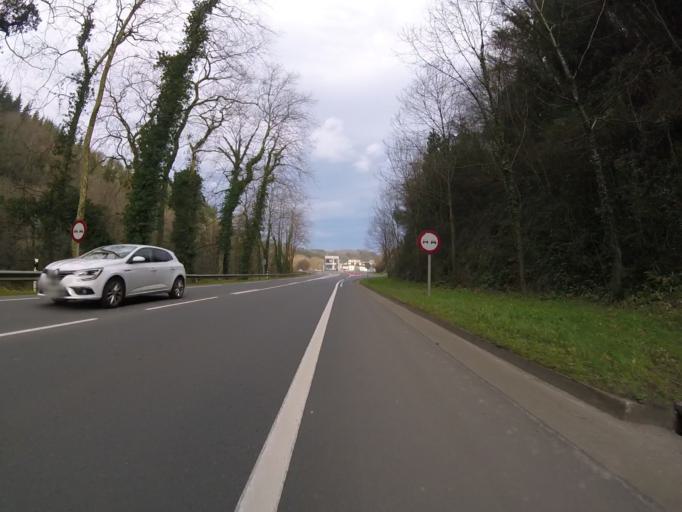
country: ES
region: Basque Country
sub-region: Provincia de Guipuzcoa
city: Cestona
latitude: 43.2505
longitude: -2.2609
